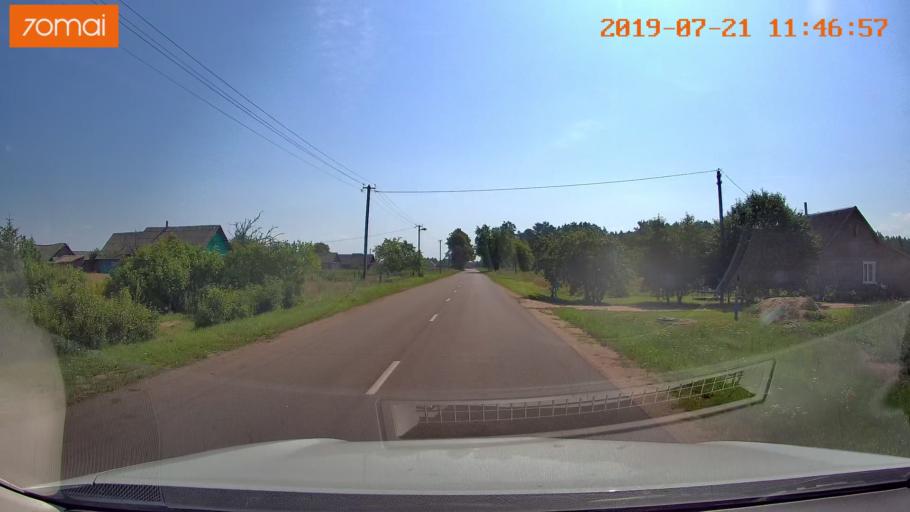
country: BY
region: Grodnenskaya
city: Lyubcha
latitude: 53.9050
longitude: 26.0389
